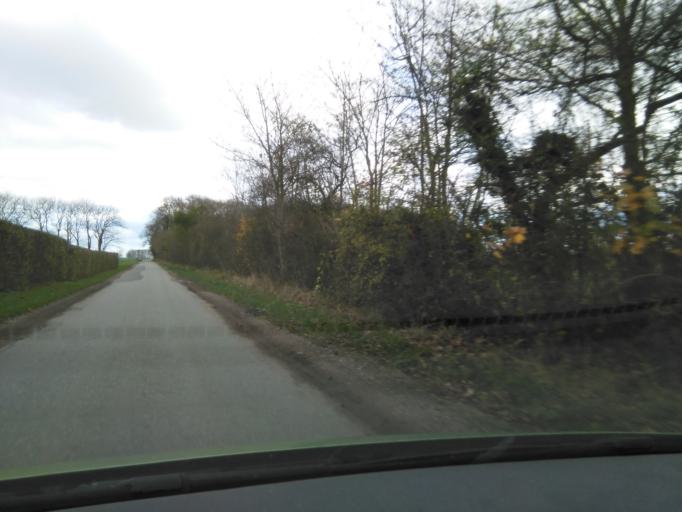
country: DK
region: Central Jutland
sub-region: Odder Kommune
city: Odder
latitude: 55.8723
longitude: 10.1706
